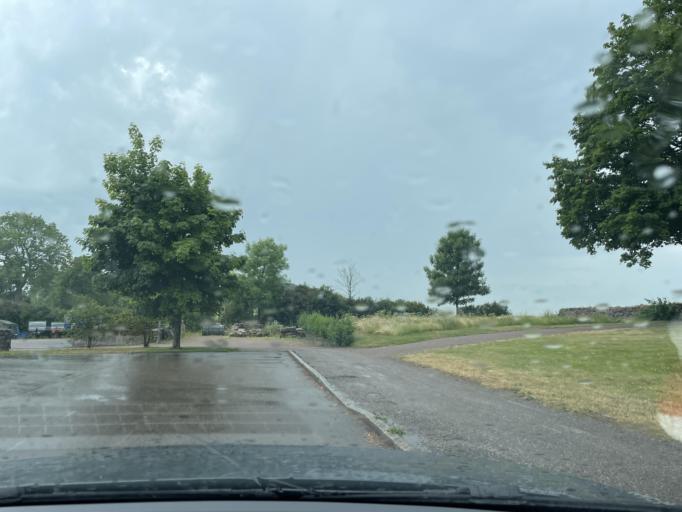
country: SE
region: OEstergoetland
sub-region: Linkopings Kommun
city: Berg
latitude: 58.4817
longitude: 15.5162
